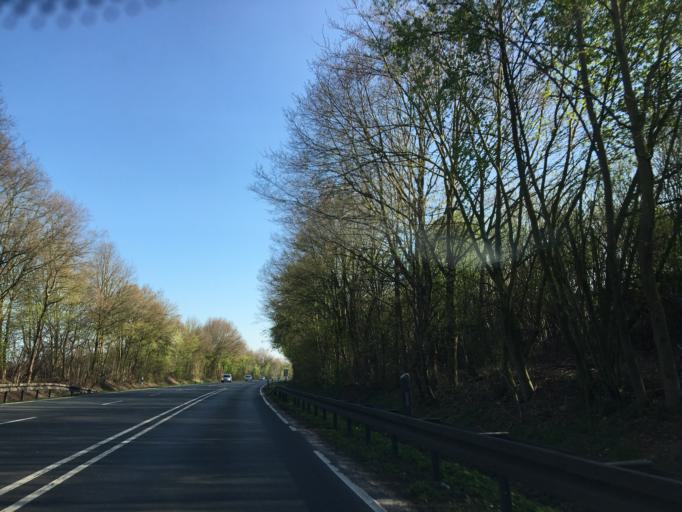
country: DE
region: North Rhine-Westphalia
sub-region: Regierungsbezirk Munster
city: Greven
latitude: 52.1037
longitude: 7.6283
